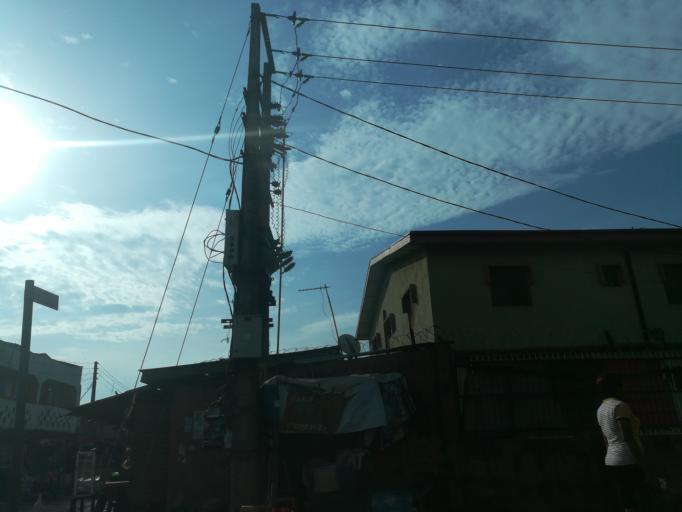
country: NG
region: Lagos
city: Ojota
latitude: 6.6029
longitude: 3.4189
